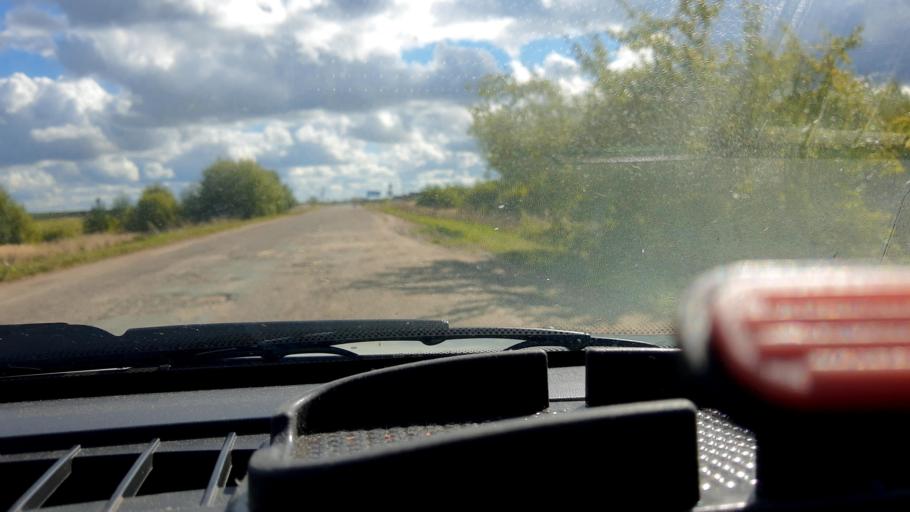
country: RU
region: Nizjnij Novgorod
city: Sharanga
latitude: 56.9395
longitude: 46.6491
